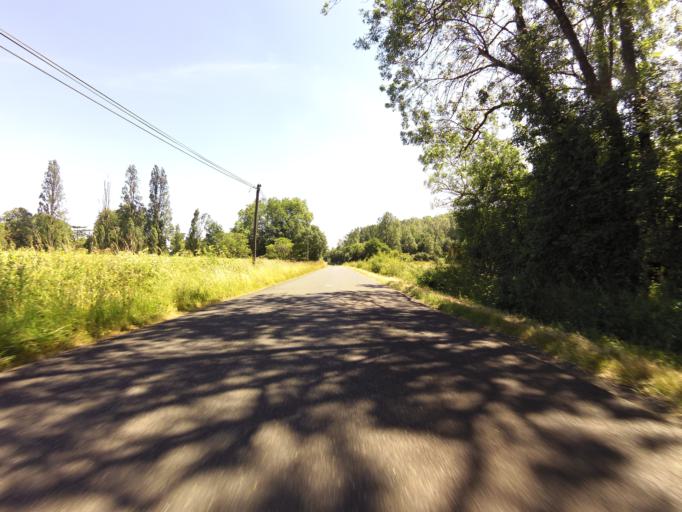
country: FR
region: Pays de la Loire
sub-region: Departement de la Loire-Atlantique
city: Le Loroux-Bottereau
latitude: 47.2085
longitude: -1.3659
